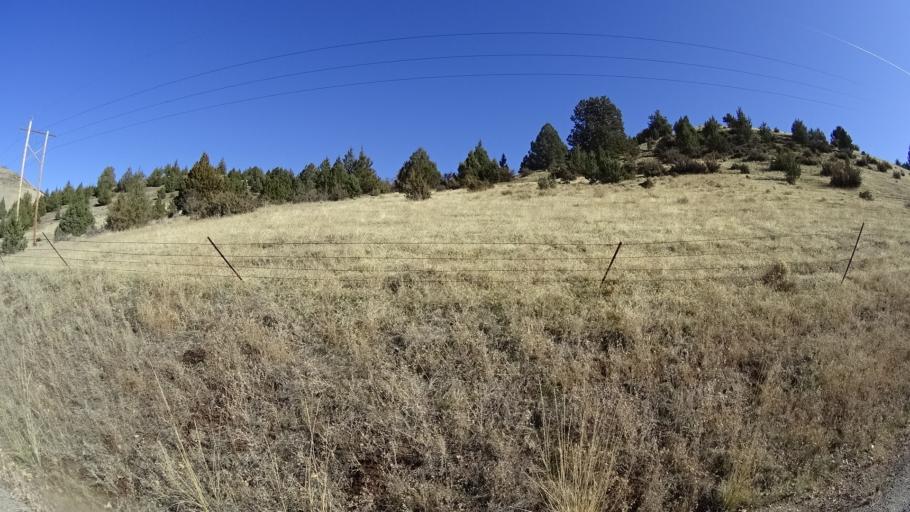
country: US
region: California
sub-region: Siskiyou County
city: Montague
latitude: 41.7887
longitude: -122.3594
